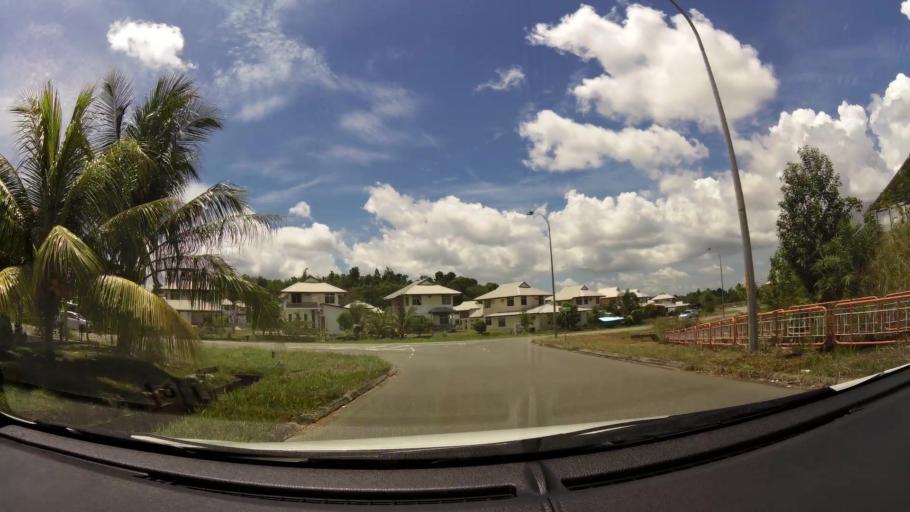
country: BN
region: Brunei and Muara
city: Bandar Seri Begawan
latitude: 4.9684
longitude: 114.9029
